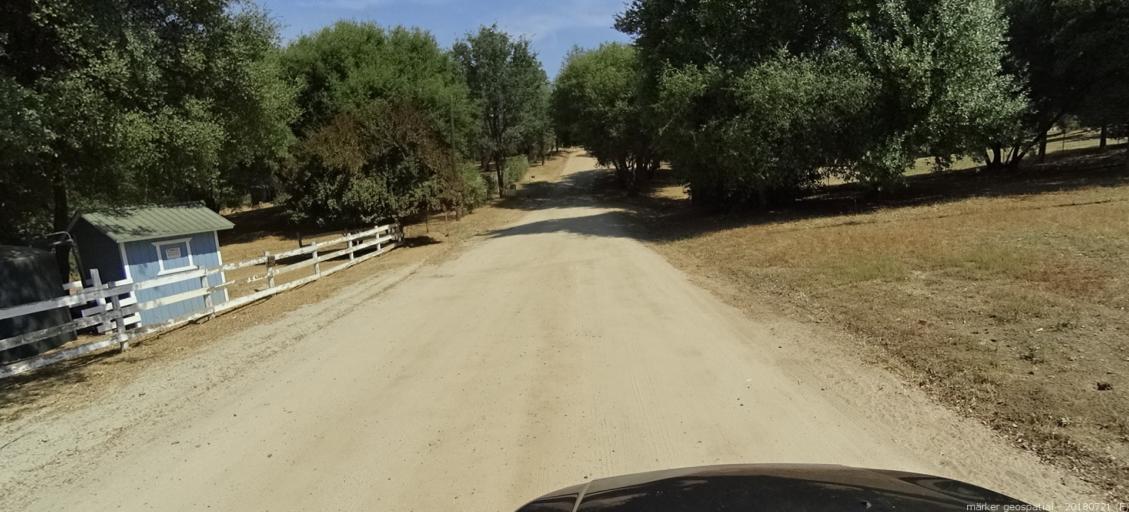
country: US
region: California
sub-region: Fresno County
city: Auberry
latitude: 37.2100
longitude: -119.5382
